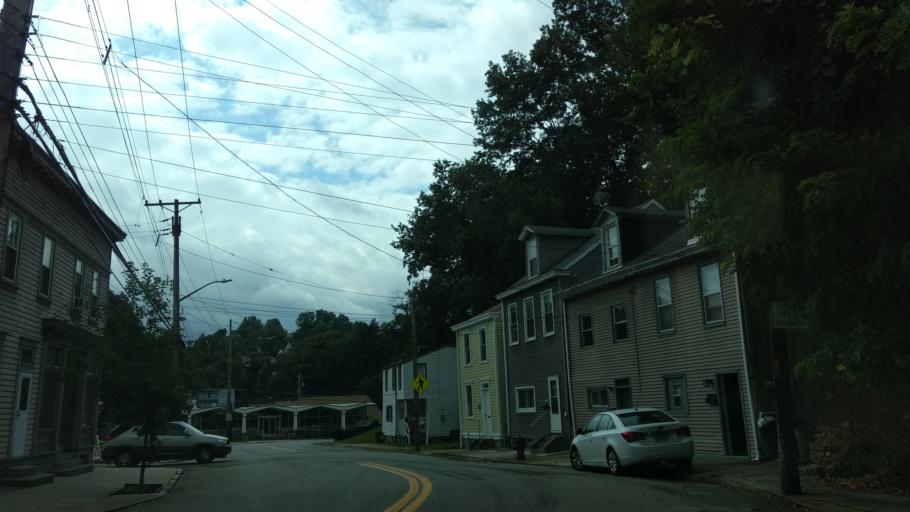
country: US
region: Pennsylvania
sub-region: Allegheny County
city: Bellevue
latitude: 40.4773
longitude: -80.0299
